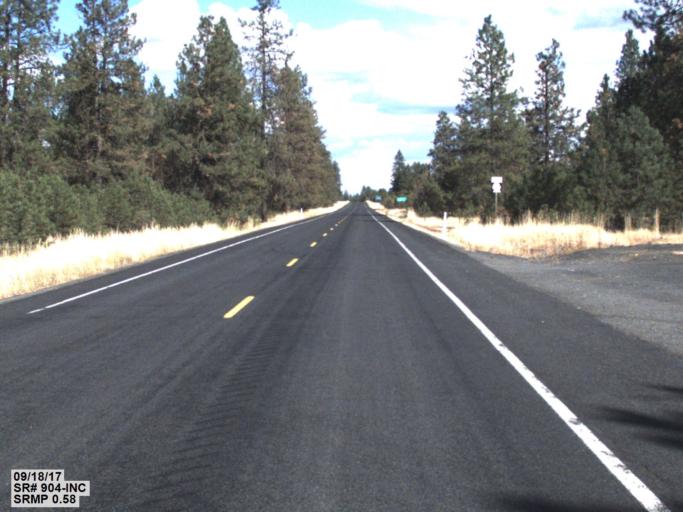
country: US
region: Washington
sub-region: Spokane County
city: Medical Lake
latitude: 47.4363
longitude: -117.7792
